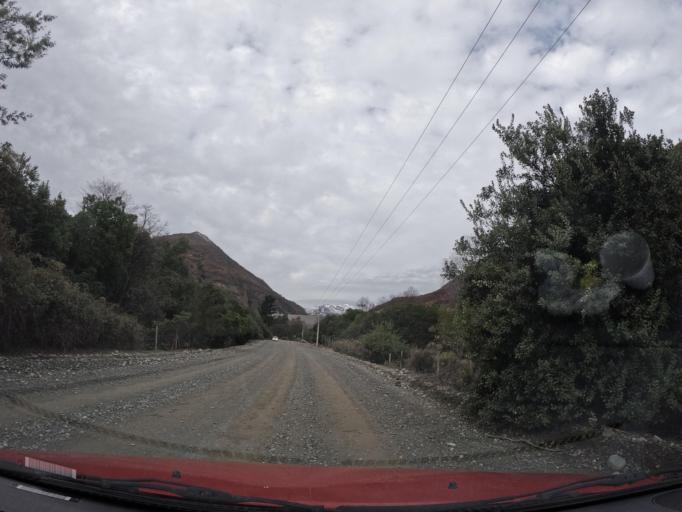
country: CL
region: Maule
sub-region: Provincia de Linares
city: Colbun
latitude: -35.8561
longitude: -71.1977
